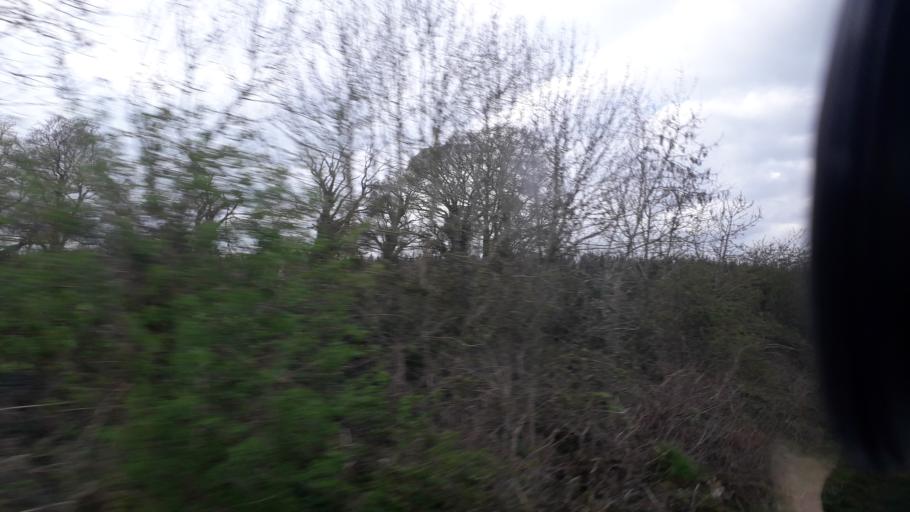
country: IE
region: Leinster
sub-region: An Iarmhi
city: An Muileann gCearr
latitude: 53.5889
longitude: -7.3850
